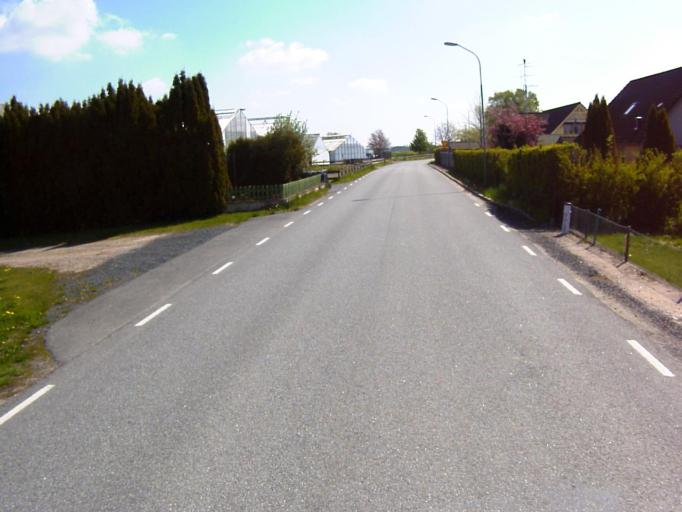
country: SE
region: Skane
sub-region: Kristianstads Kommun
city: Fjalkinge
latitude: 56.0176
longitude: 14.2309
